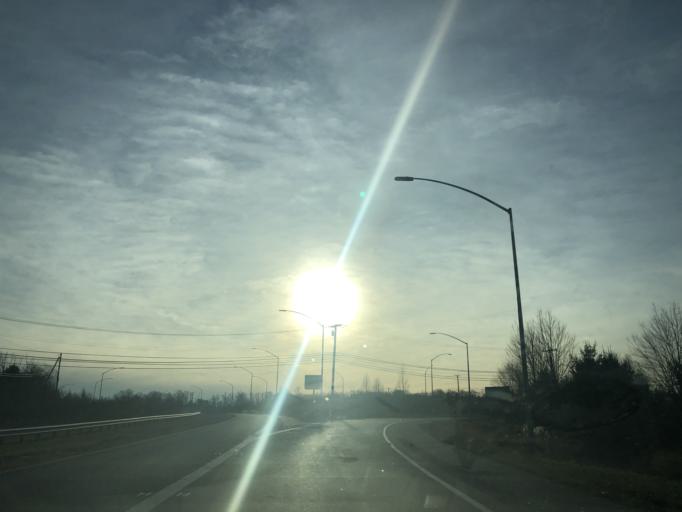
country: US
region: Maryland
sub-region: Carroll County
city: Sykesville
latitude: 39.2770
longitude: -76.9847
